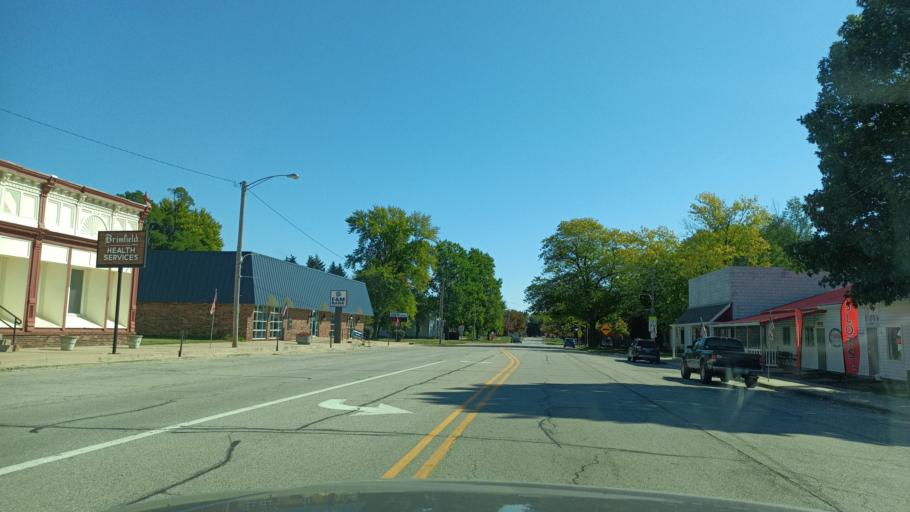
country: US
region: Illinois
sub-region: Peoria County
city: Elmwood
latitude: 40.8388
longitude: -89.8845
